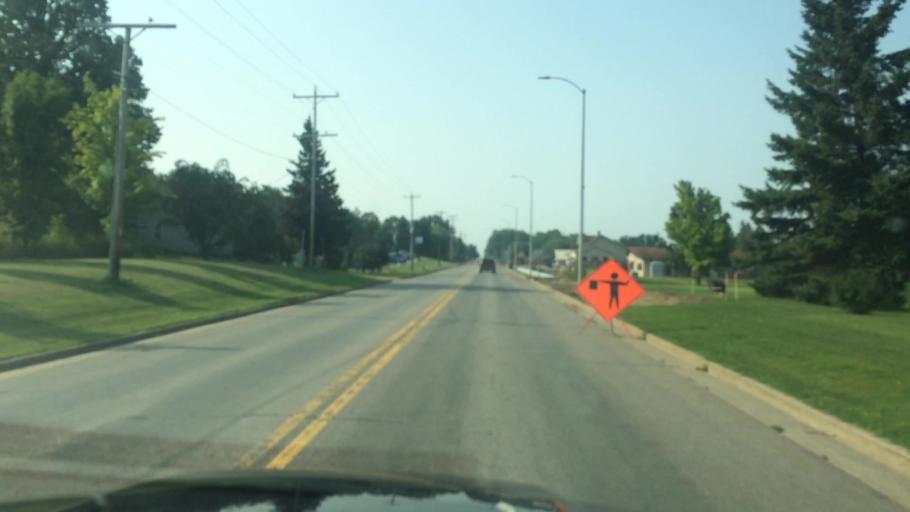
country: US
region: Wisconsin
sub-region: Marathon County
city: Stratford
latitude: 44.8111
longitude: -90.0792
